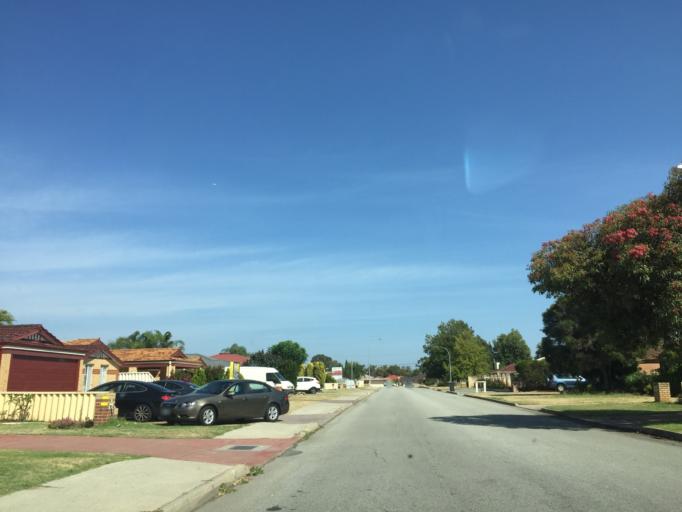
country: AU
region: Western Australia
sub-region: Gosnells
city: Thornlie
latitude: -32.0795
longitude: 115.9588
